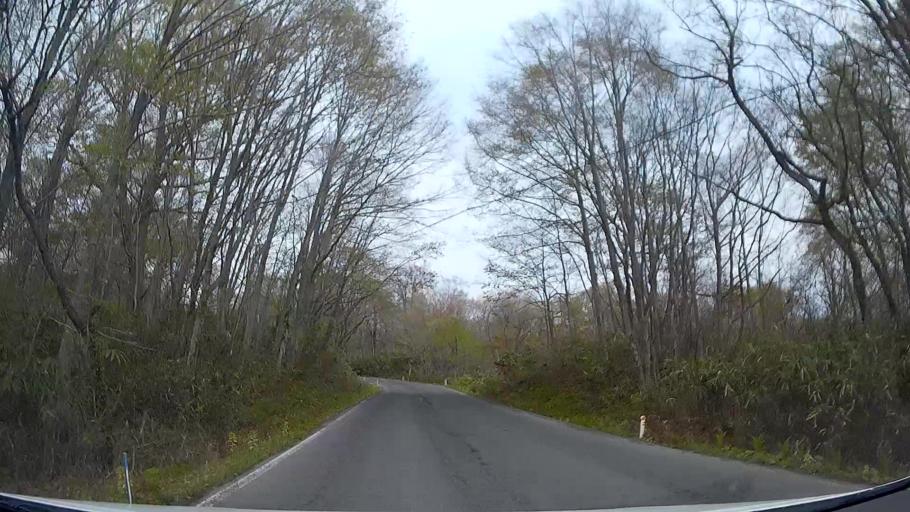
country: JP
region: Akita
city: Hanawa
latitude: 40.4033
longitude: 140.8661
